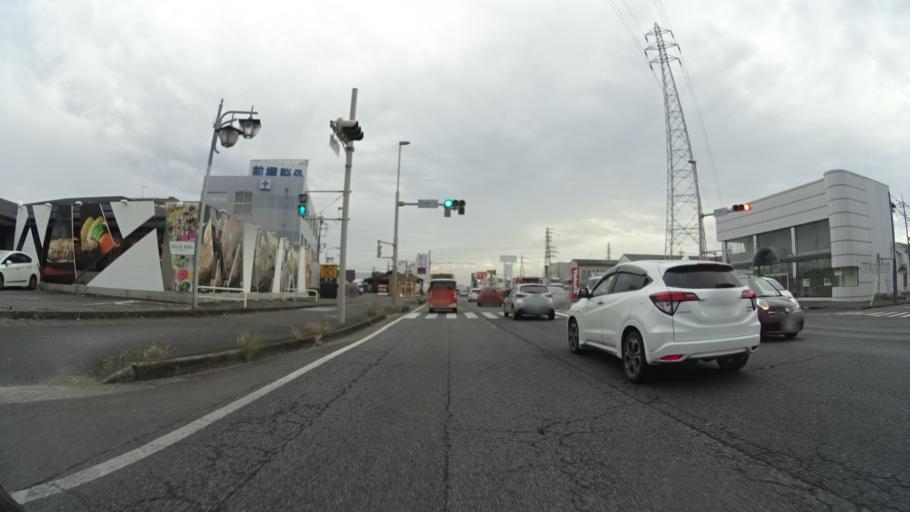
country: JP
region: Gunma
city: Maebashi-shi
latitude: 36.3816
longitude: 139.1014
